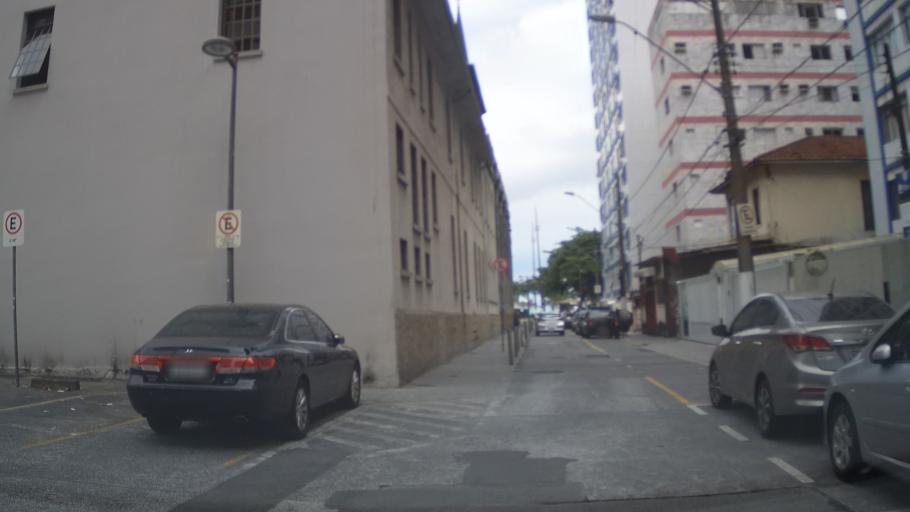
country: BR
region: Sao Paulo
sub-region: Santos
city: Santos
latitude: -23.9736
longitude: -46.3197
